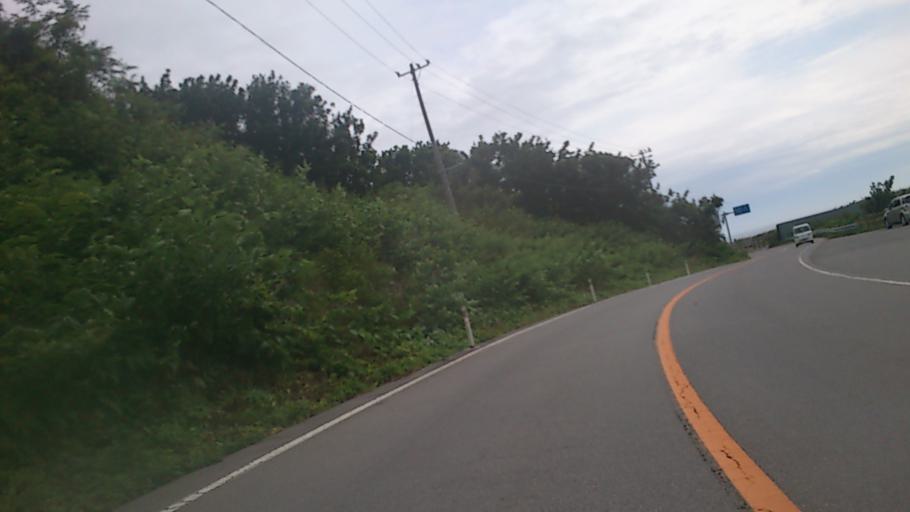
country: JP
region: Akita
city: Noshiromachi
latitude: 40.4304
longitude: 139.9414
